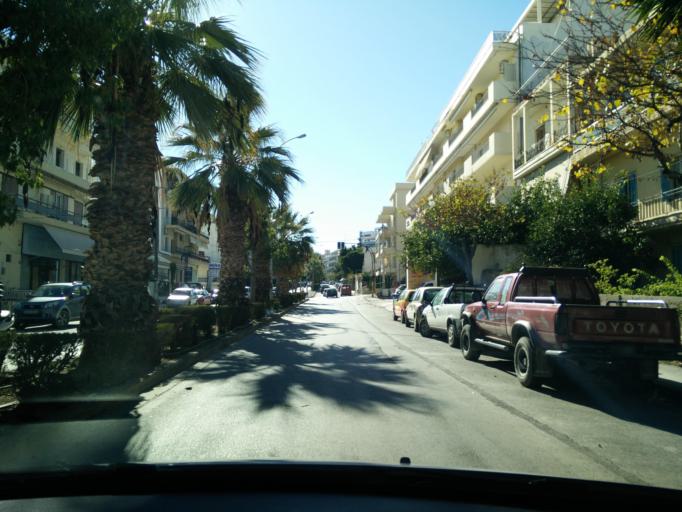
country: GR
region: Crete
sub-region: Nomos Irakleiou
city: Irakleion
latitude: 35.3322
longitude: 25.1400
